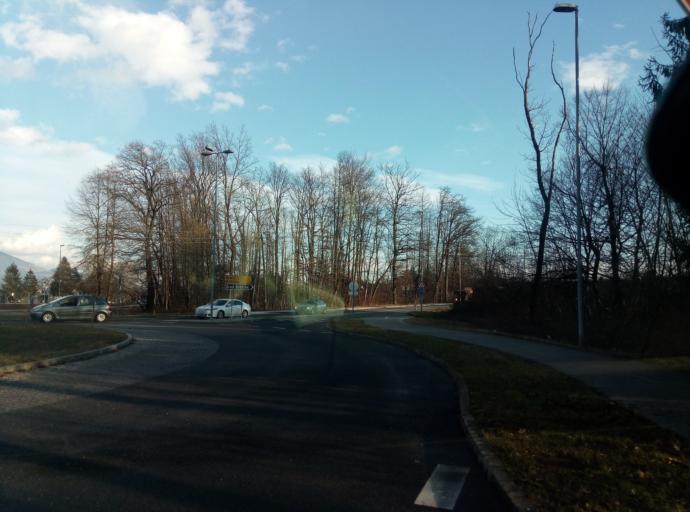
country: SI
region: Kranj
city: Kokrica
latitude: 46.2671
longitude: 14.3516
